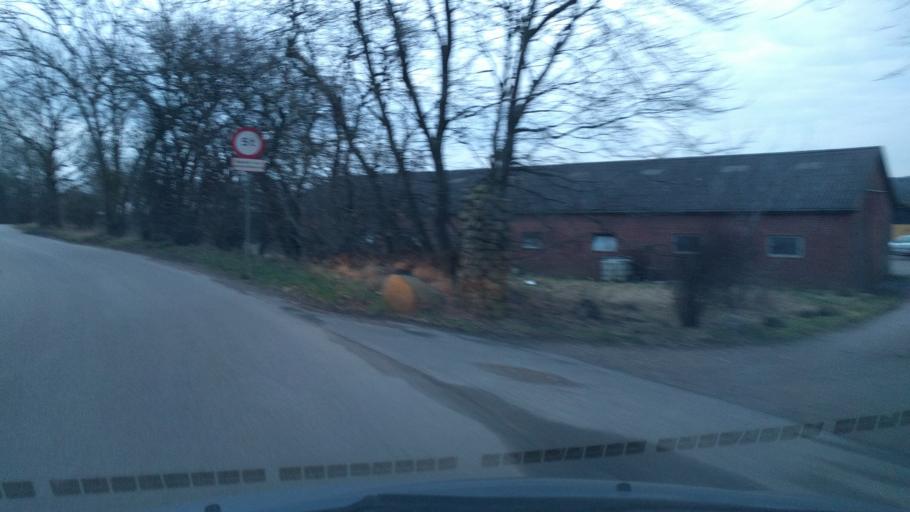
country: DK
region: South Denmark
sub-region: Haderslev Kommune
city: Haderslev
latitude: 55.2590
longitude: 9.4228
